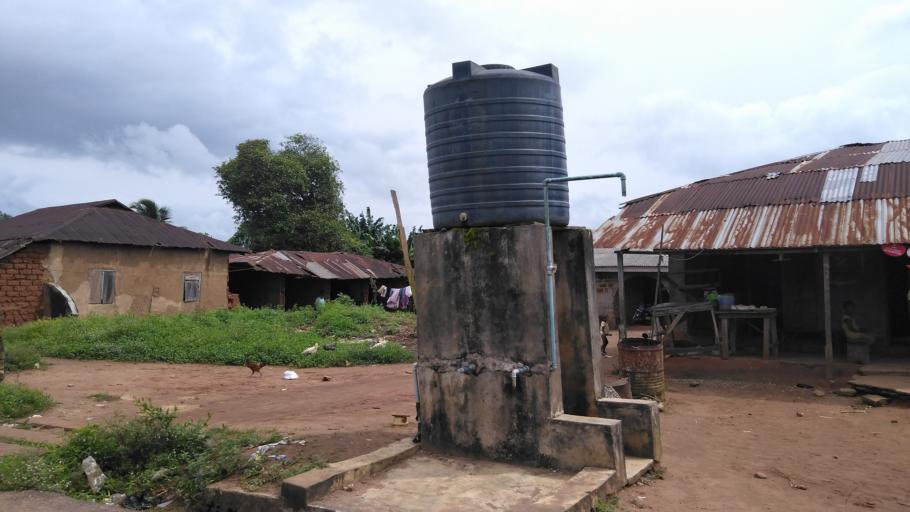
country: NG
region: Ogun
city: Abigi
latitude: 6.5988
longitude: 4.4934
